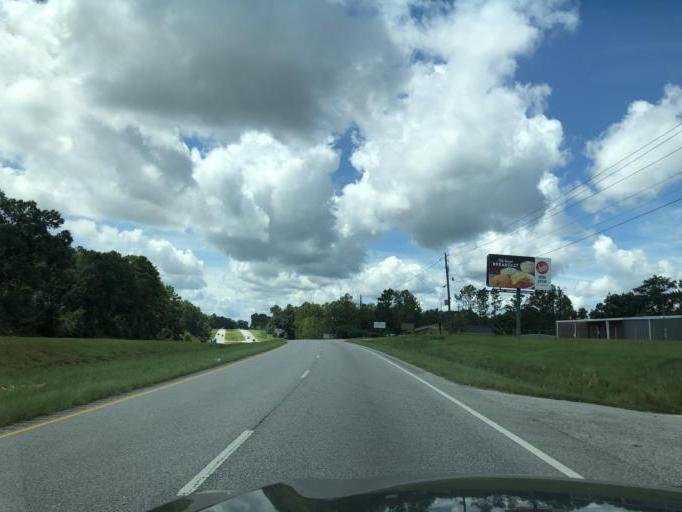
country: US
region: Alabama
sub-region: Barbour County
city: Eufaula
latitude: 31.9372
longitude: -85.1355
